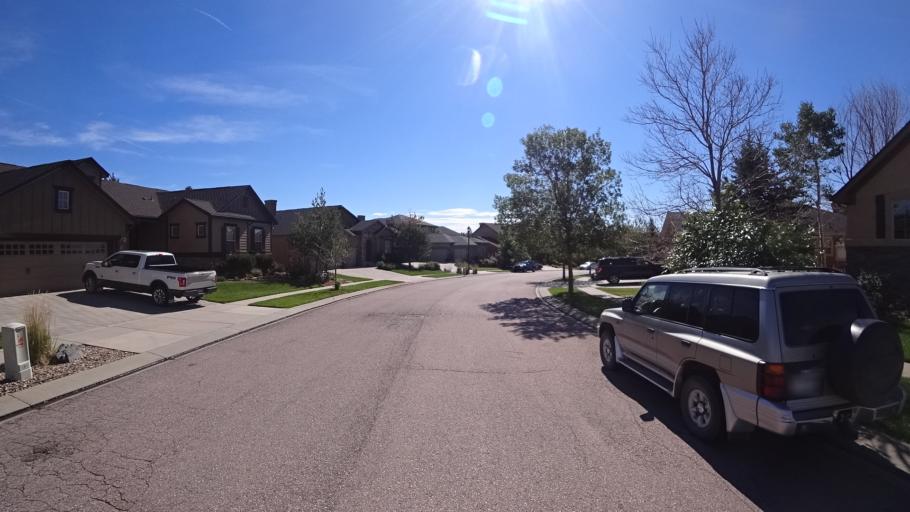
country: US
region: Colorado
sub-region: El Paso County
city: Gleneagle
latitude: 39.0265
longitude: -104.8062
